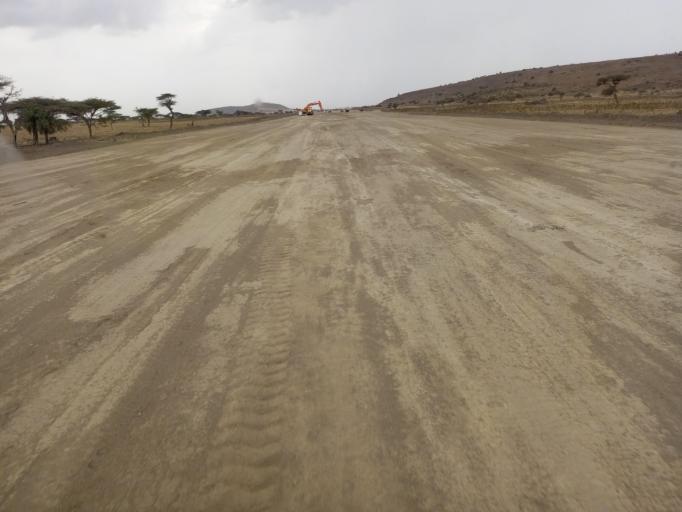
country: ET
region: Oromiya
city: Ziway
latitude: 7.8182
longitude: 38.6451
